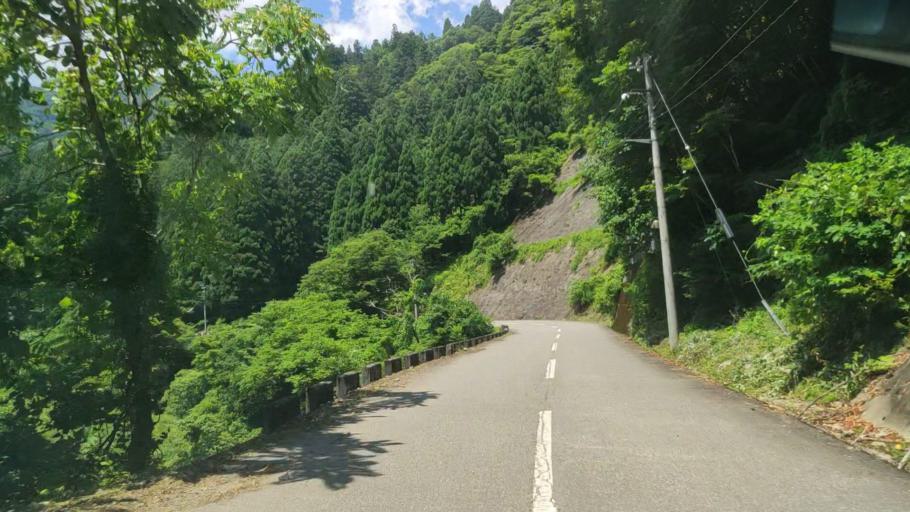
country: JP
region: Fukui
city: Ono
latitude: 35.8747
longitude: 136.5008
